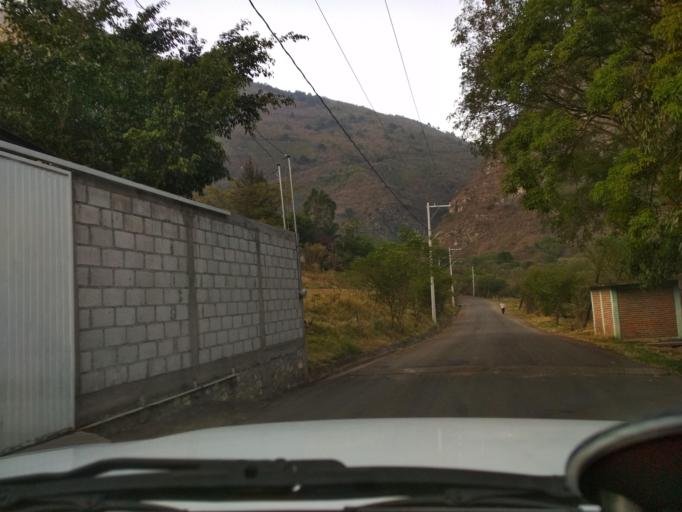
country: MX
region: Veracruz
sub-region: Nogales
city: Taza de Agua Ojo Zarco
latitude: 18.7750
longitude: -97.1954
